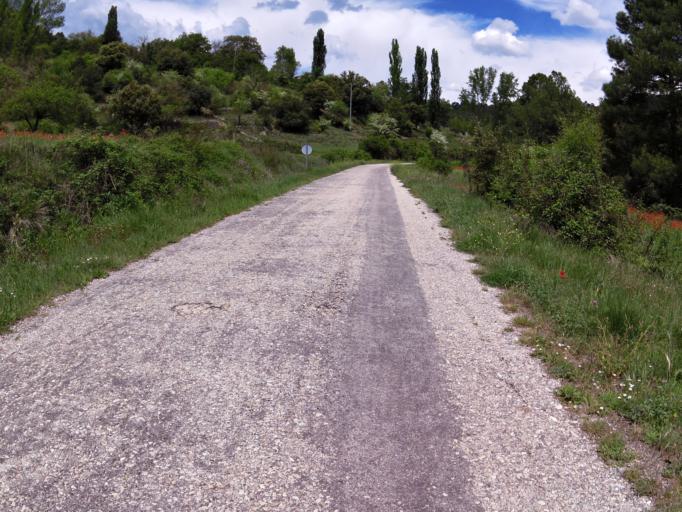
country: ES
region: Castille-La Mancha
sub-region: Provincia de Albacete
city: Paterna del Madera
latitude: 38.5760
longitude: -2.3376
